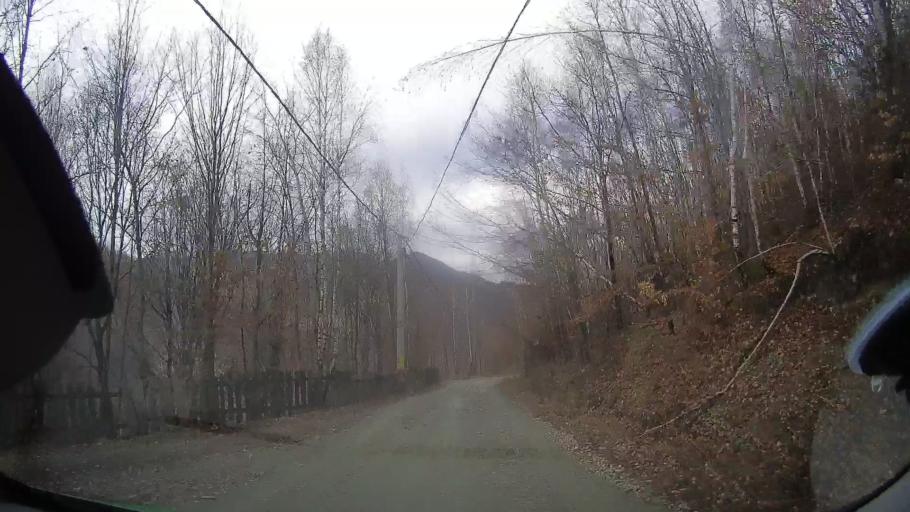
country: RO
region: Cluj
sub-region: Comuna Valea Ierii
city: Valea Ierii
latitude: 46.6817
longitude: 23.3086
